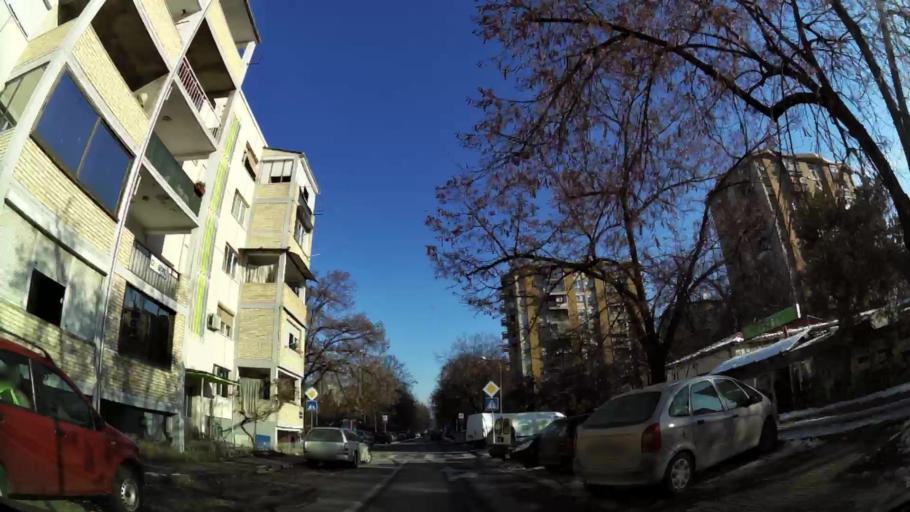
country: MK
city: Krushopek
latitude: 42.0057
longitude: 21.3862
